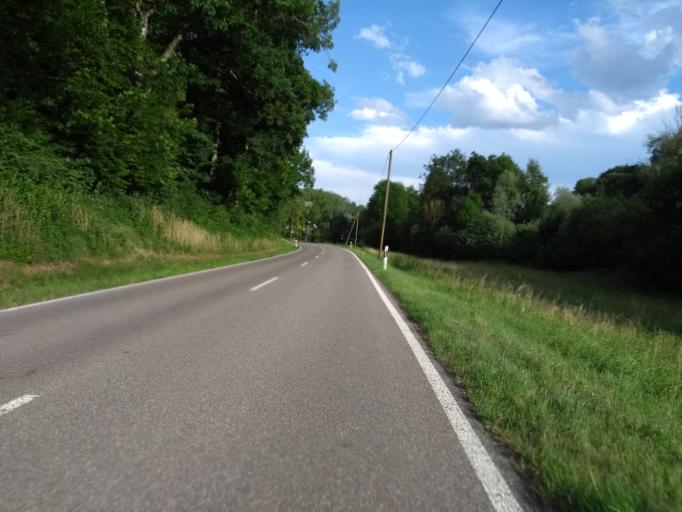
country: DE
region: Baden-Wuerttemberg
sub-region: Tuebingen Region
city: Dornstadt
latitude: 48.4290
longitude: 9.8927
